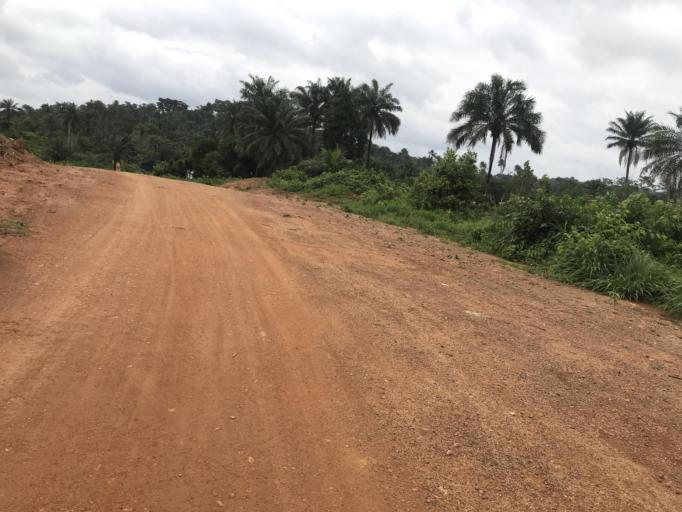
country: SL
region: Eastern Province
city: Kailahun
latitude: 8.3187
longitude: -10.5218
